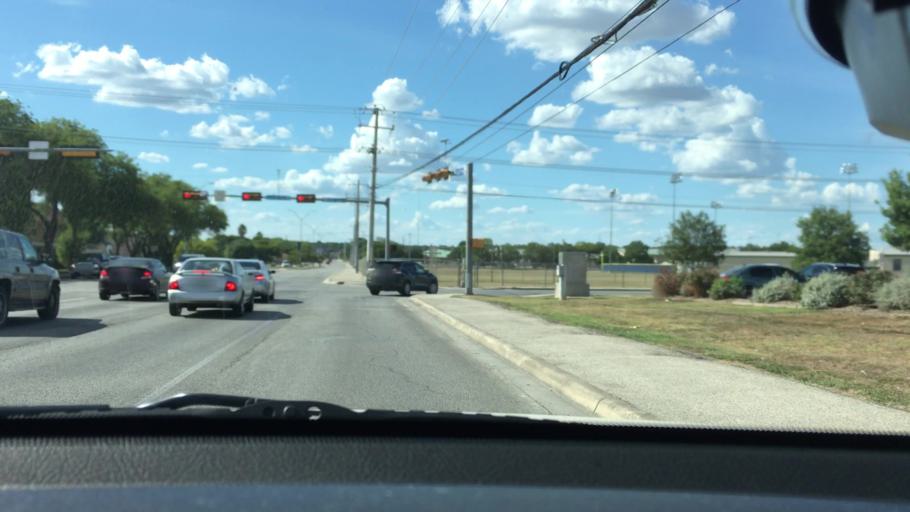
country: US
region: Texas
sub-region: Guadalupe County
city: Schertz
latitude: 29.5606
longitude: -98.2671
